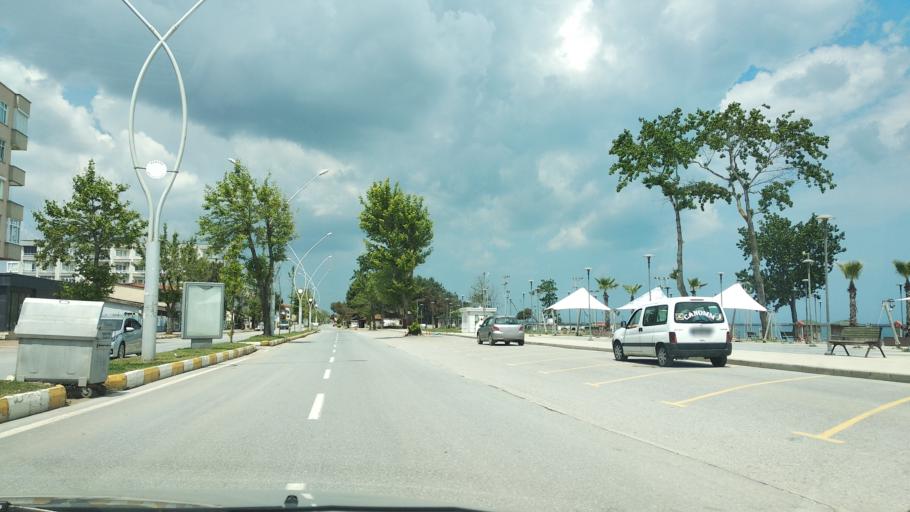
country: TR
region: Sakarya
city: Karasu
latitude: 41.1107
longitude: 30.6913
